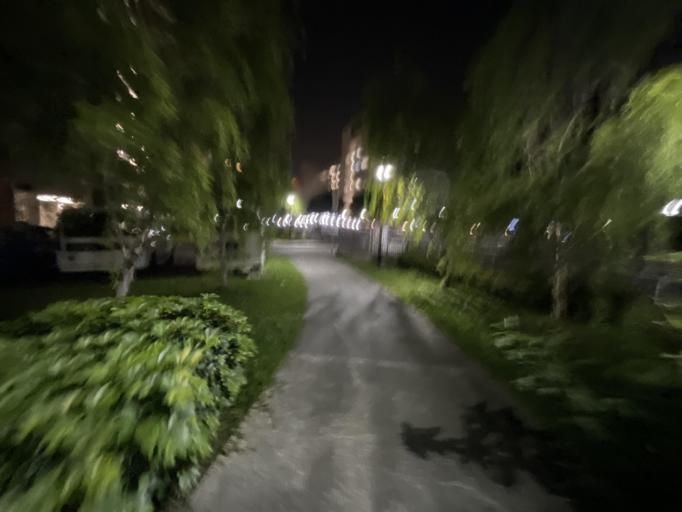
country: SG
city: Singapore
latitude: 1.3043
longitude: 103.7684
